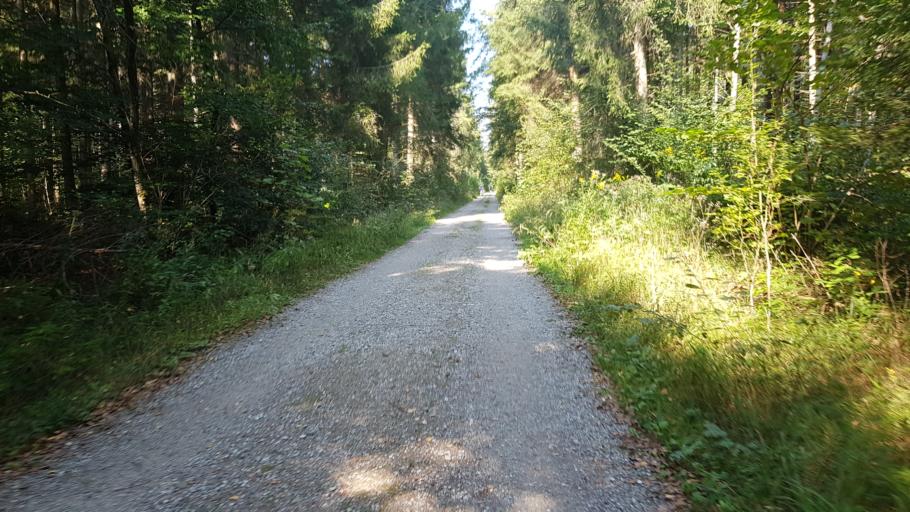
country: DE
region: Bavaria
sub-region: Upper Bavaria
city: Krailling
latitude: 48.0966
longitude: 11.3890
